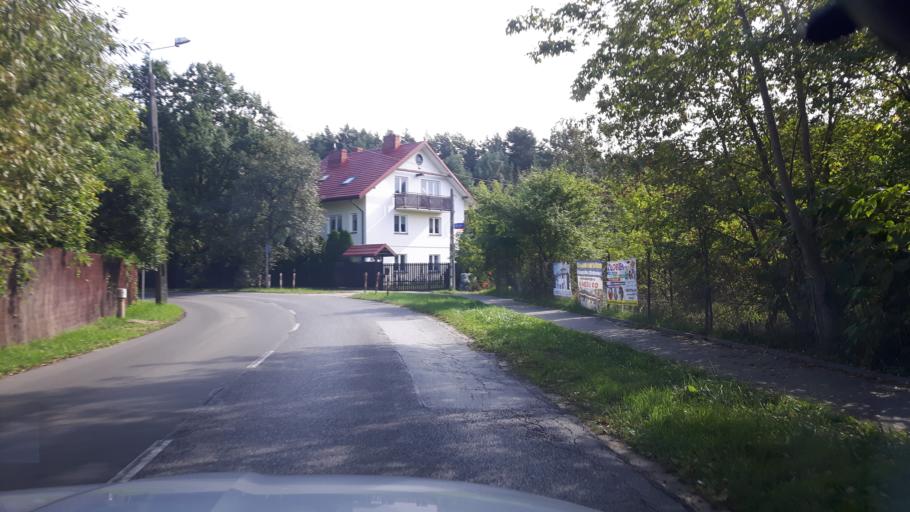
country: PL
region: Masovian Voivodeship
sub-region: Powiat legionowski
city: Stanislawow Pierwszy
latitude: 52.3611
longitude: 21.0500
